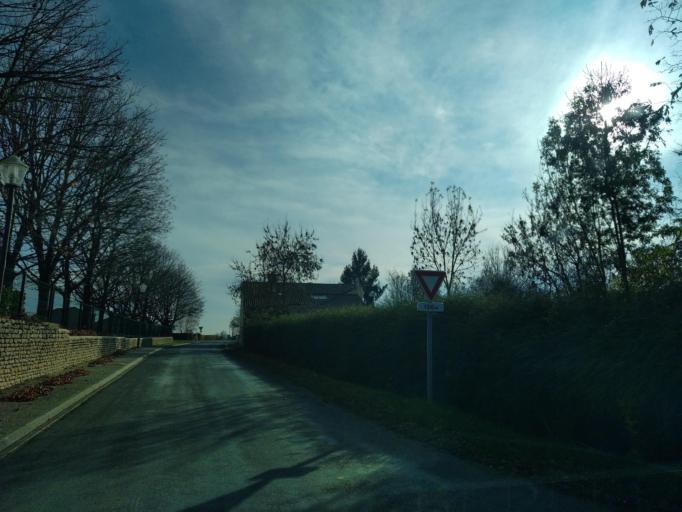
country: FR
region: Pays de la Loire
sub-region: Departement de la Vendee
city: Maillezais
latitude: 46.3689
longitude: -0.7417
